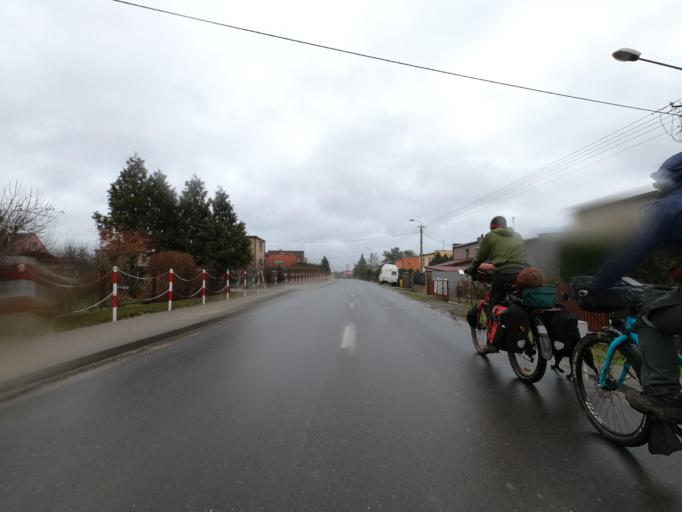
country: PL
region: Greater Poland Voivodeship
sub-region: Powiat pilski
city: Osiek nad Notecia
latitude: 53.1177
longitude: 17.2751
